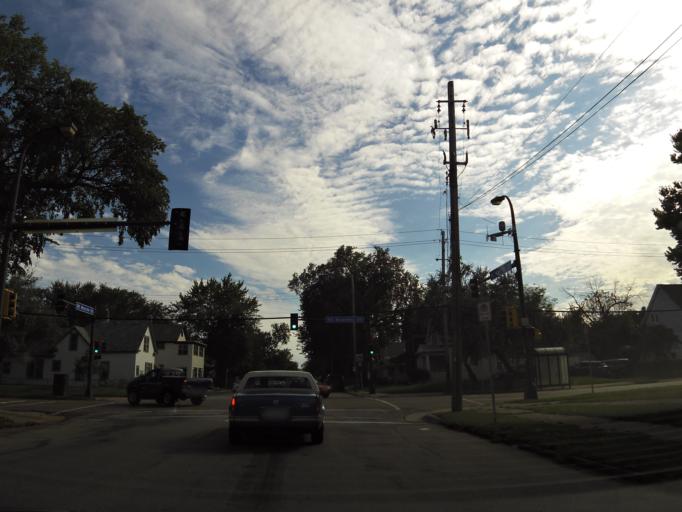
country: US
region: Minnesota
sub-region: Hennepin County
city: Minneapolis
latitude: 44.9990
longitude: -93.2525
